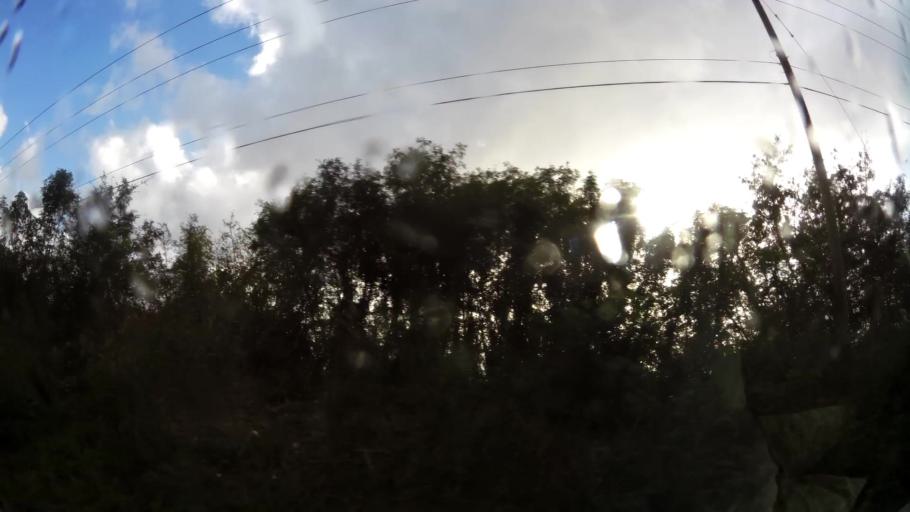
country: DM
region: Saint Paul
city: Mahaut
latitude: 15.3799
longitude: -61.4093
